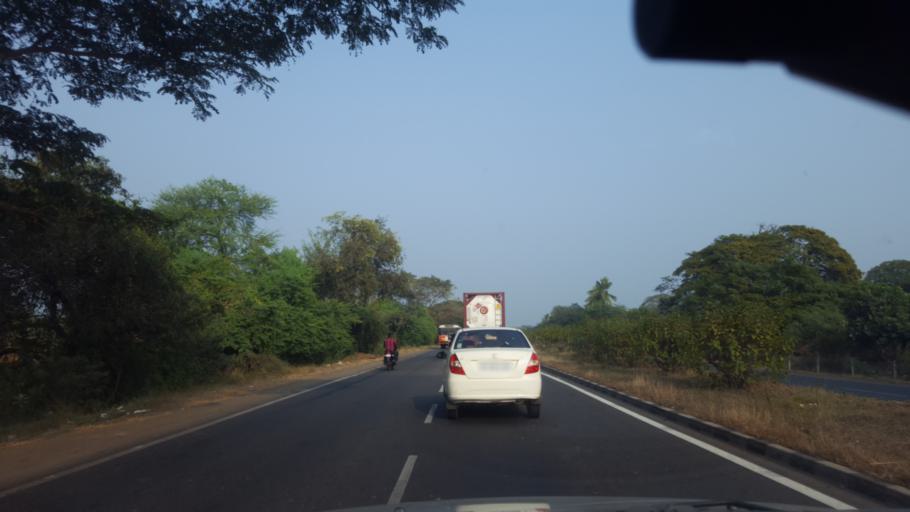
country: IN
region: Andhra Pradesh
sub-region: West Godavari
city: Tadepallegudem
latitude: 16.8175
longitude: 81.3870
